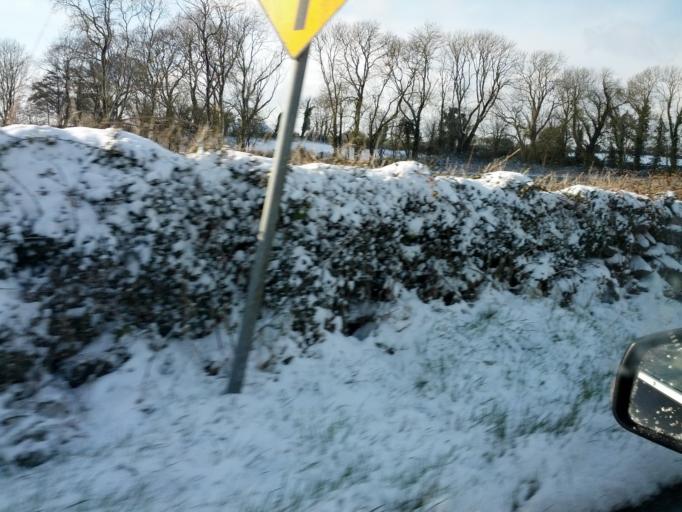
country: IE
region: Connaught
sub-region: County Galway
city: Athenry
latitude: 53.2027
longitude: -8.7610
